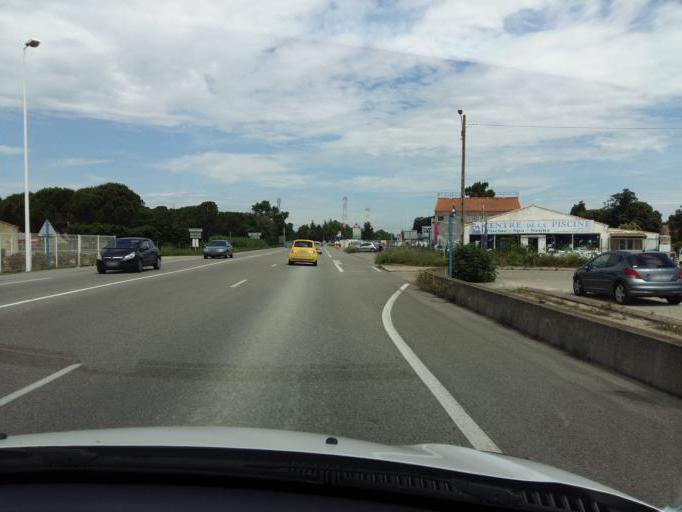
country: FR
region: Rhone-Alpes
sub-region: Departement de la Drome
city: Saint-Paul-Trois-Chateaux
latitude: 44.3252
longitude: 4.7411
